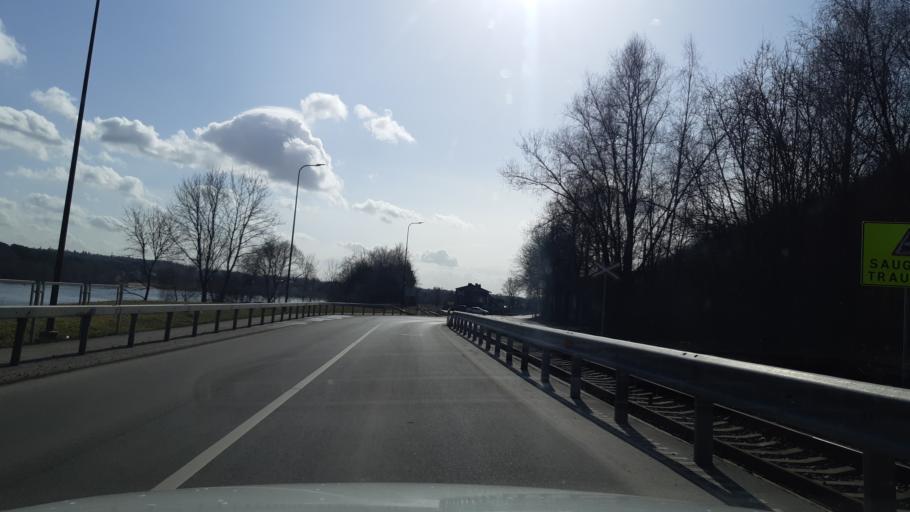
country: LT
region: Kauno apskritis
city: Dainava (Kaunas)
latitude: 54.8826
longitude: 23.9568
